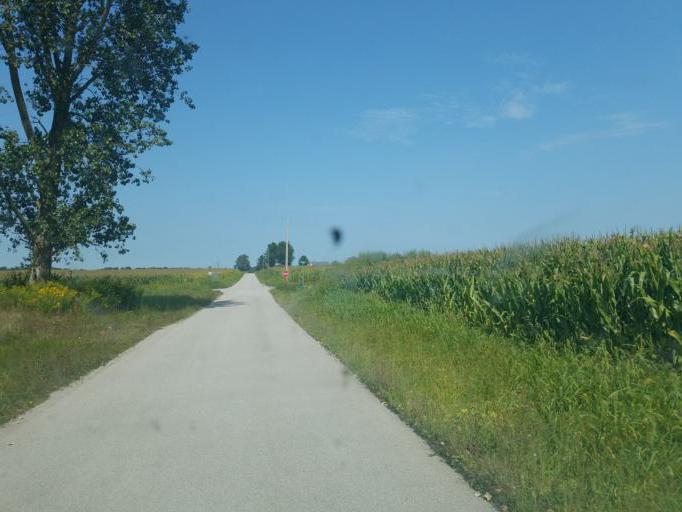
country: US
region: Ohio
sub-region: Crawford County
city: Bucyrus
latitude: 40.7745
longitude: -83.1118
